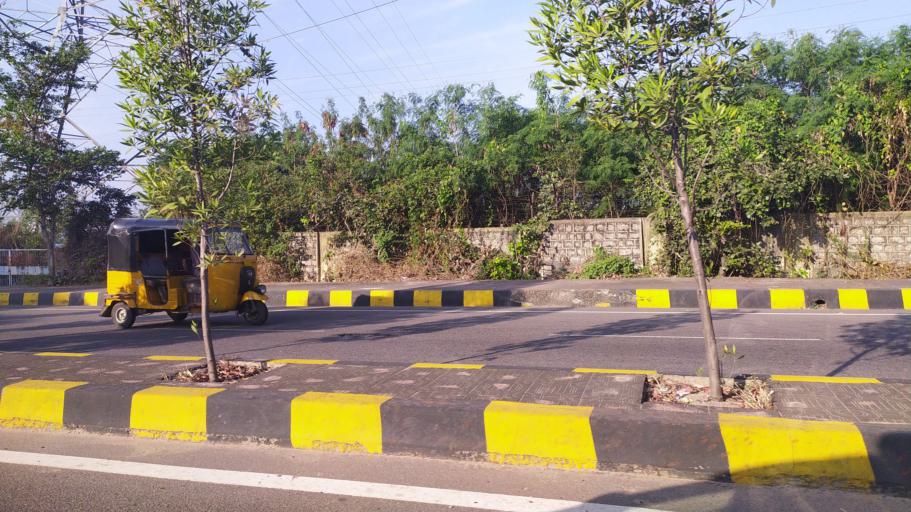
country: IN
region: Telangana
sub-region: Hyderabad
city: Hyderabad
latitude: 17.3293
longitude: 78.4092
